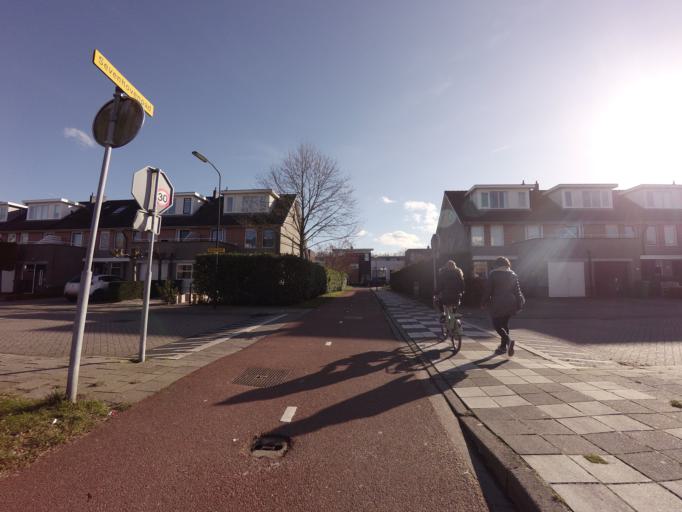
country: NL
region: Utrecht
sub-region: Gemeente IJsselstein
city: IJsselstein
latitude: 52.0086
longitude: 5.0474
